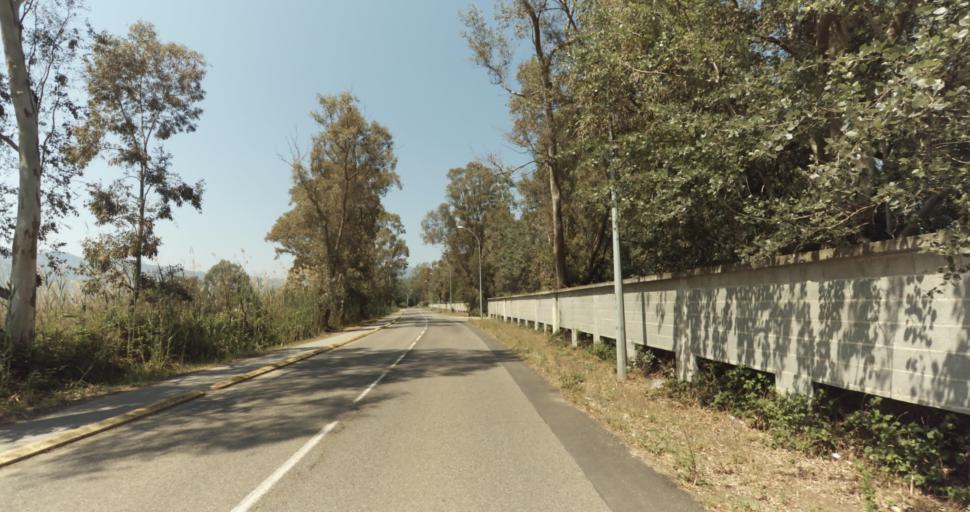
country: FR
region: Corsica
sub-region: Departement de la Haute-Corse
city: Biguglia
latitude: 42.6129
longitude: 9.4808
